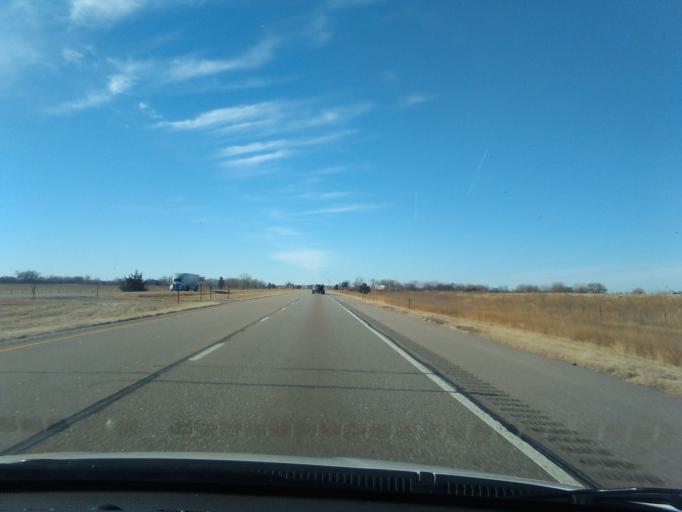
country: US
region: Nebraska
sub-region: Hall County
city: Wood River
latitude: 40.8026
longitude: -98.4793
